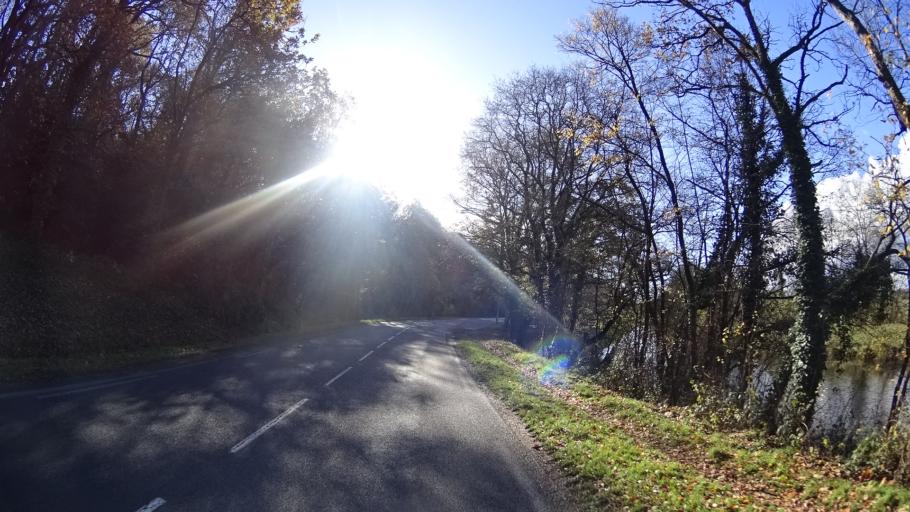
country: FR
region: Brittany
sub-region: Departement du Morbihan
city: Saint-Perreux
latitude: 47.6694
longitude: -2.0883
